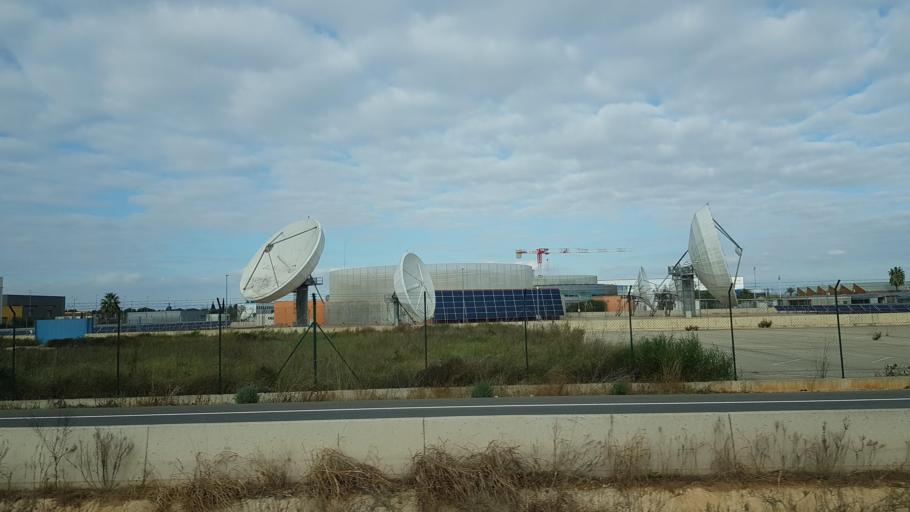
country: ES
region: Valencia
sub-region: Provincia de Valencia
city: Manises
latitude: 39.4764
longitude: -0.4868
